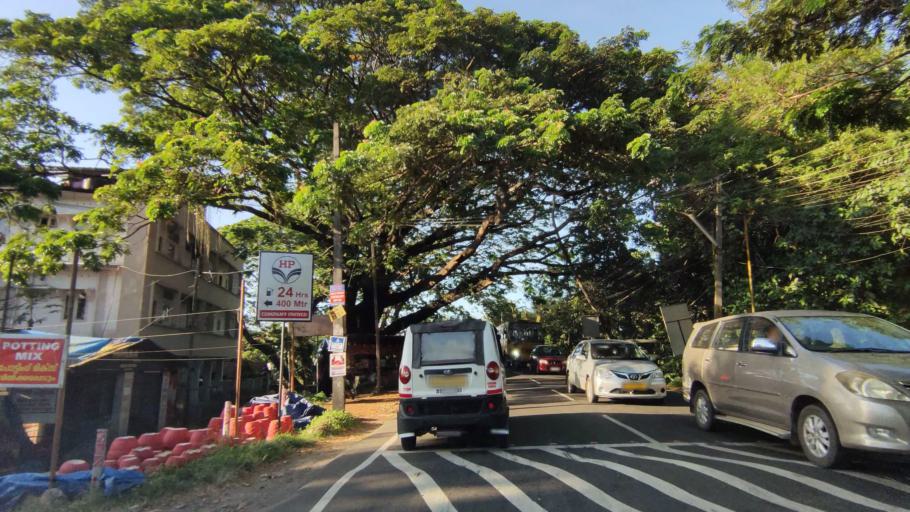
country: IN
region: Kerala
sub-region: Kottayam
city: Kottayam
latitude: 9.6003
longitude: 76.5176
